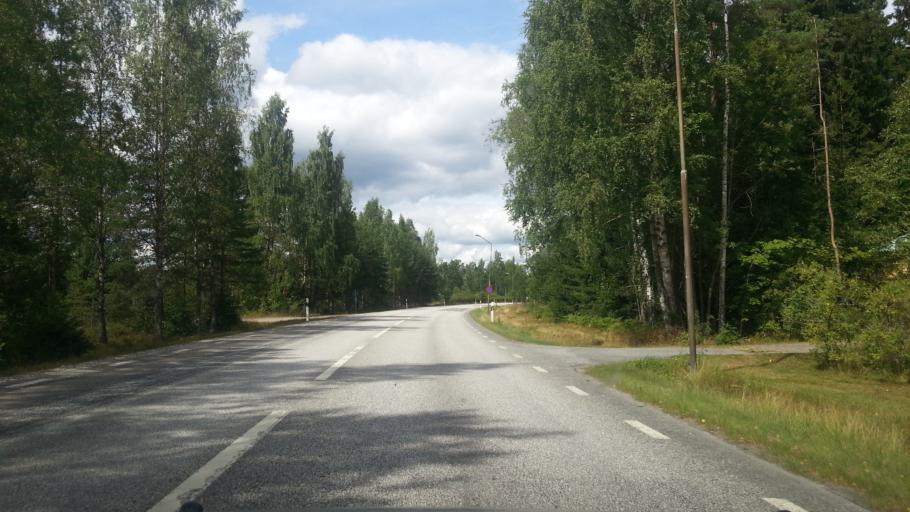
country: SE
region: Vaestmanland
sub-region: Skinnskattebergs Kommun
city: Skinnskatteberg
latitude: 59.8109
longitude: 15.5309
